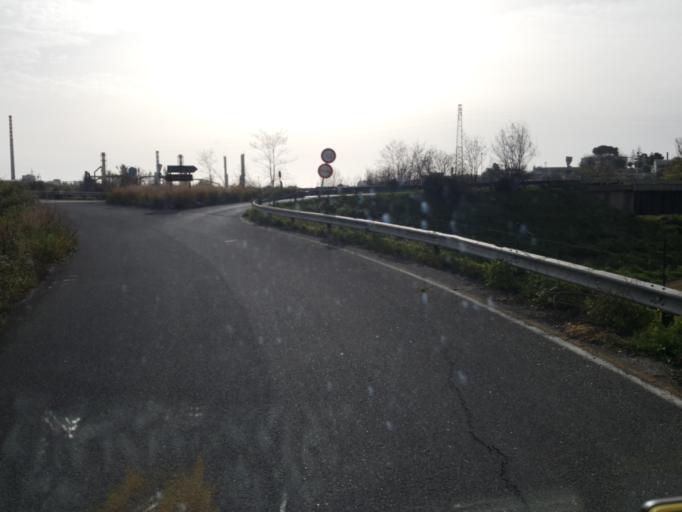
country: IT
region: Sicily
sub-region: Provincia di Siracusa
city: Melilli
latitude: 37.2200
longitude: 15.1646
